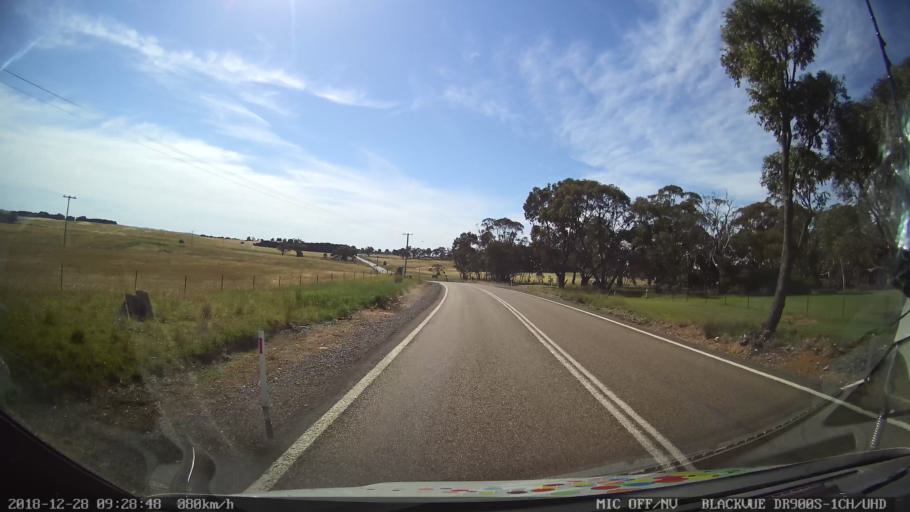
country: AU
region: New South Wales
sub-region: Upper Lachlan Shire
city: Crookwell
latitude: -34.4417
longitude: 149.4200
